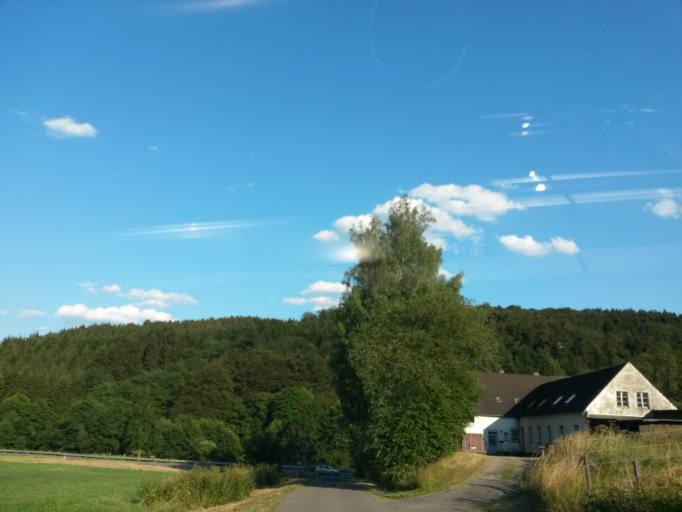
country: DE
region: North Rhine-Westphalia
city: Meinerzhagen
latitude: 51.1072
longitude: 7.7090
